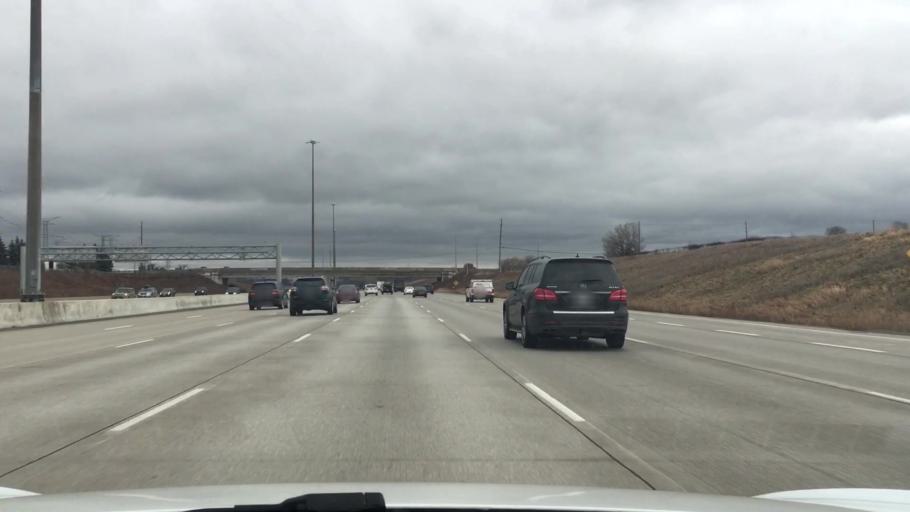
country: CA
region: Ontario
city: Etobicoke
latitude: 43.7598
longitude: -79.6093
